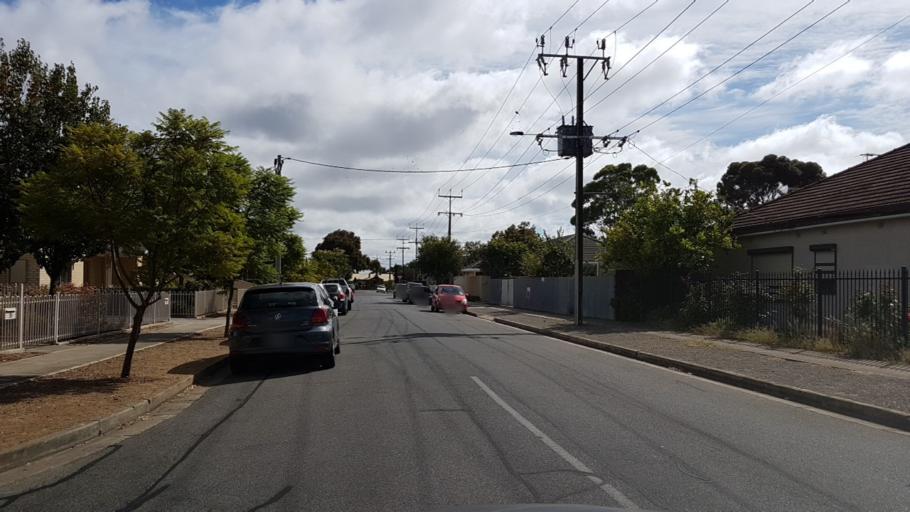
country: AU
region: South Australia
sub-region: Marion
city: Plympton Park
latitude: -34.9846
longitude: 138.5499
